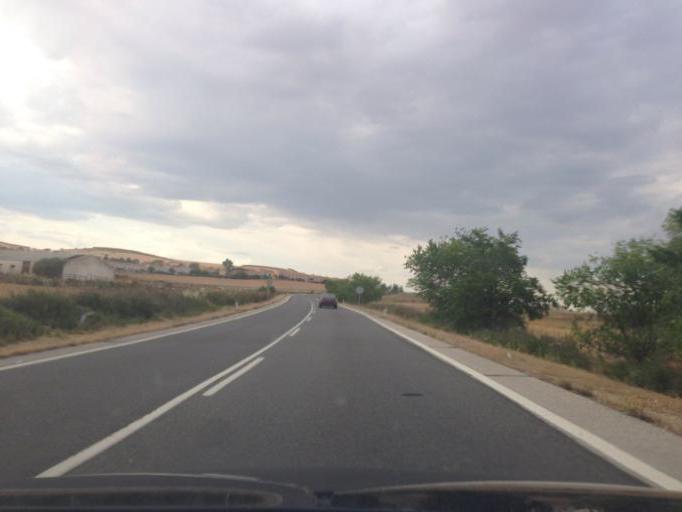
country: ES
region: Madrid
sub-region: Provincia de Madrid
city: Ajalvir
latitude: 40.5291
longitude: -3.4767
